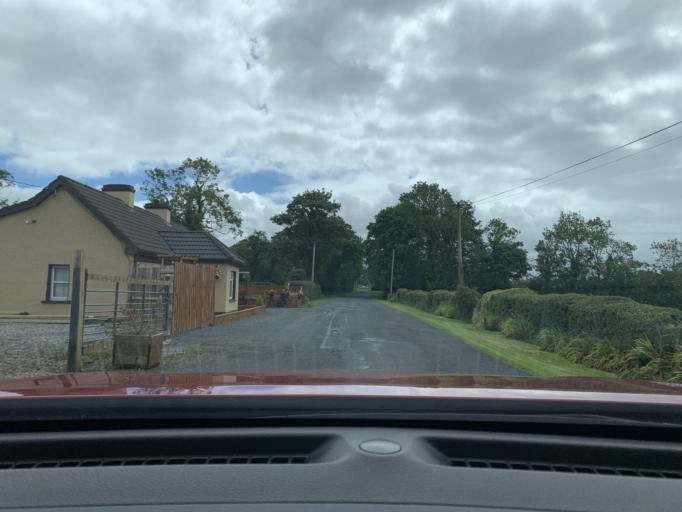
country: IE
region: Connaught
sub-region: Sligo
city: Sligo
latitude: 54.3358
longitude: -8.4722
